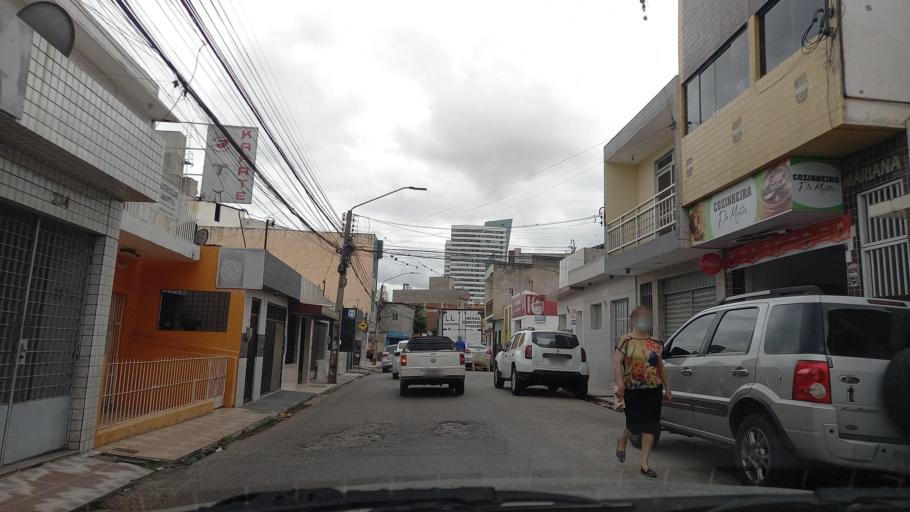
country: BR
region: Pernambuco
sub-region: Caruaru
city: Caruaru
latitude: -8.2772
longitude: -35.9657
